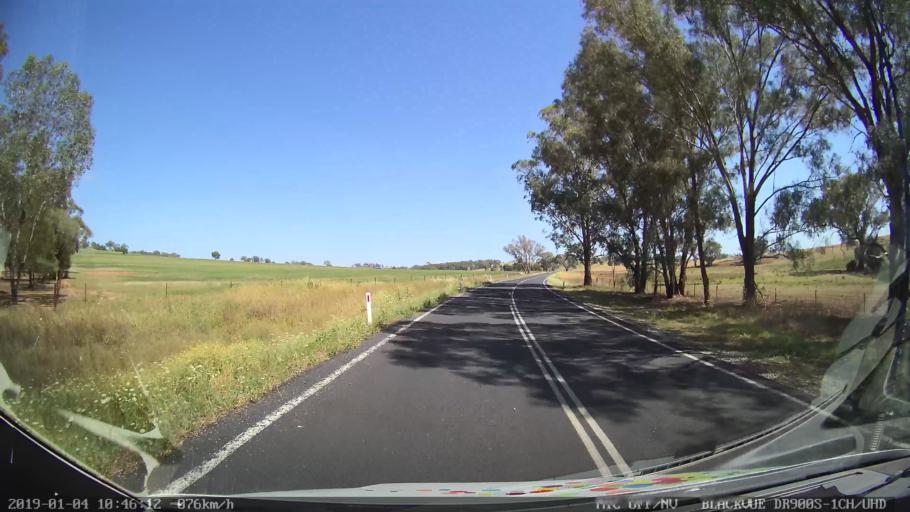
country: AU
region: New South Wales
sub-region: Cabonne
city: Molong
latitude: -33.2839
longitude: 148.7242
